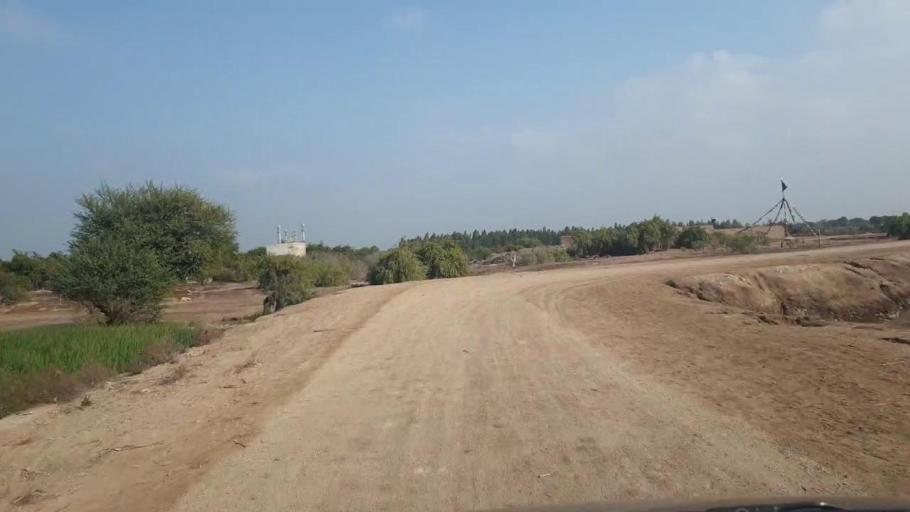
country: PK
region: Sindh
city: Shahdadpur
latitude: 25.9132
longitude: 68.6820
